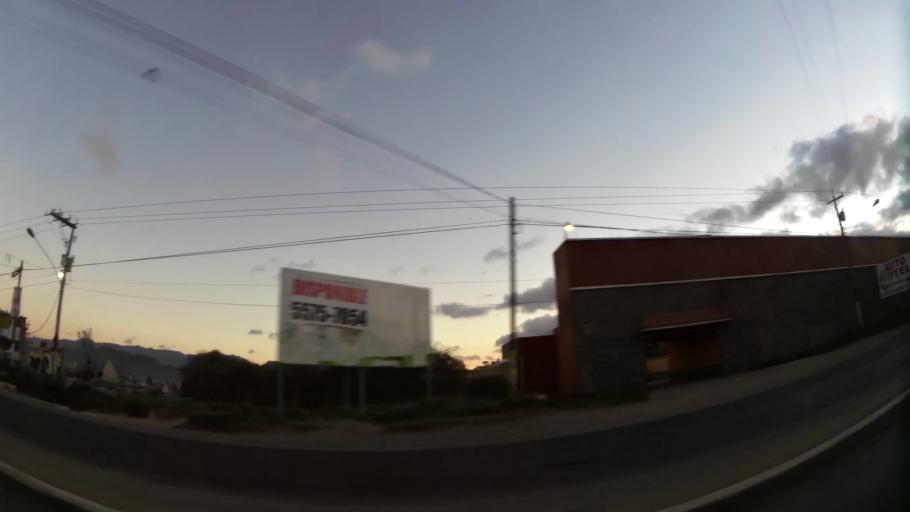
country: GT
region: Quetzaltenango
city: Olintepeque
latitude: 14.8630
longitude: -91.5349
